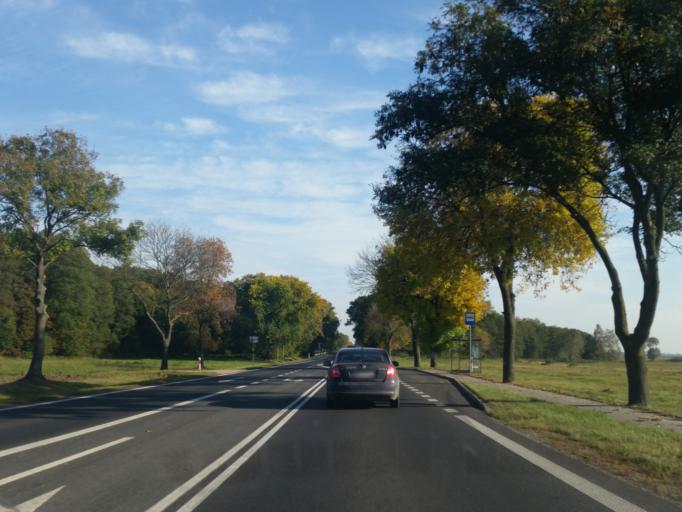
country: PL
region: Masovian Voivodeship
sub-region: Powiat sierpecki
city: Zawidz
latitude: 52.7797
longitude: 19.9057
